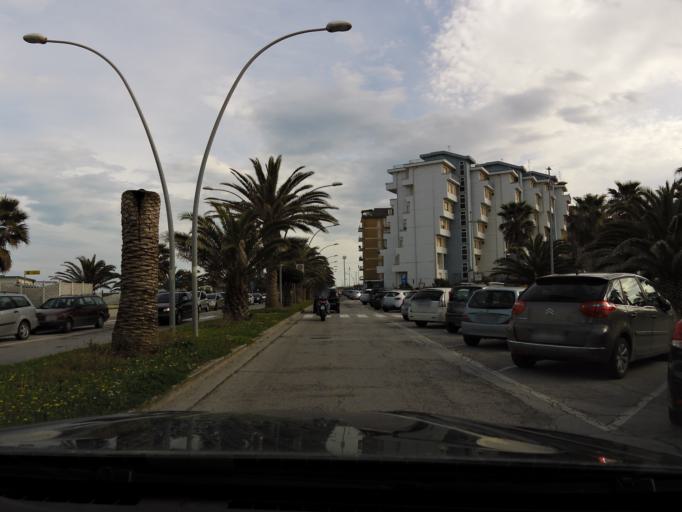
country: IT
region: The Marches
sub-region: Provincia di Macerata
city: Portocivitanova
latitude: 43.3019
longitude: 13.7373
